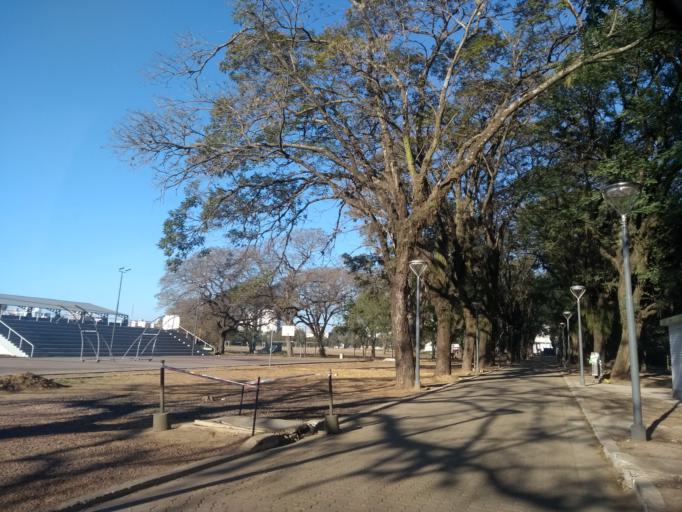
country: AR
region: Chaco
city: Resistencia
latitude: -27.4376
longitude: -58.9829
